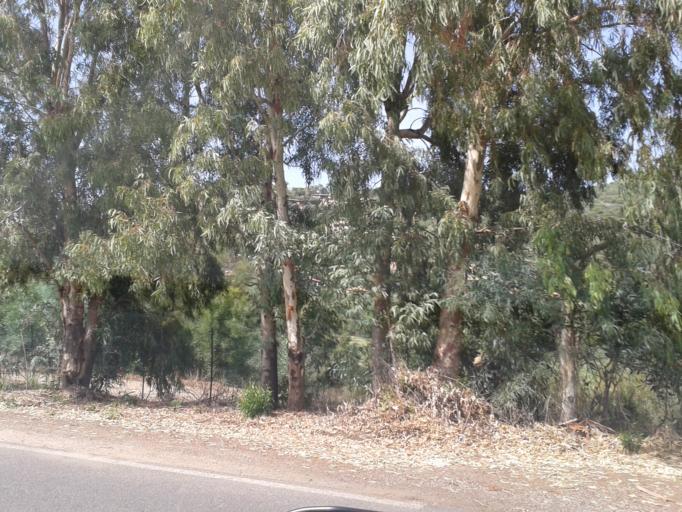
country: IT
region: Sardinia
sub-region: Provincia di Cagliari
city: Villasimius
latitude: 39.1297
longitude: 9.5101
